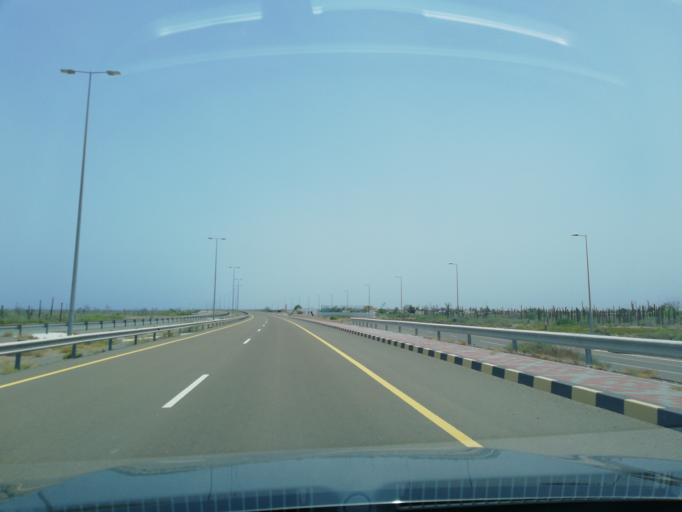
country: OM
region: Al Batinah
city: Shinas
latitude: 24.8755
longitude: 56.4056
